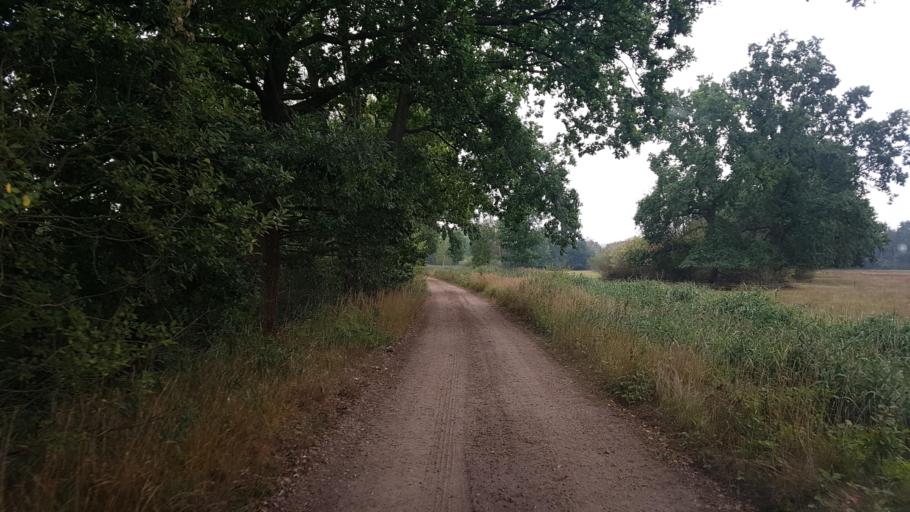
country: DE
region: Brandenburg
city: Bronkow
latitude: 51.6251
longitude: 13.9081
